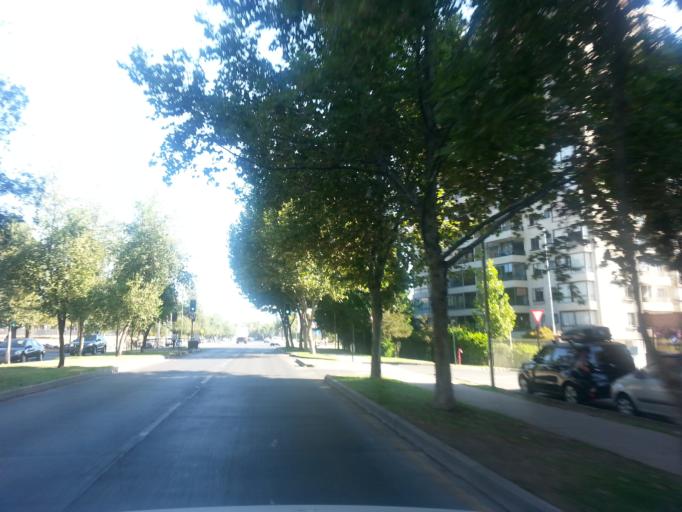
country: CL
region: Santiago Metropolitan
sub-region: Provincia de Santiago
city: Villa Presidente Frei, Nunoa, Santiago, Chile
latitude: -33.4265
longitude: -70.5387
